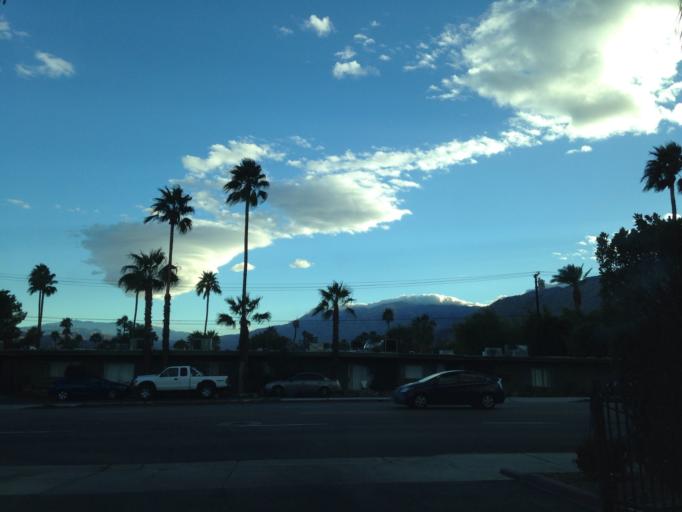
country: US
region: California
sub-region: Riverside County
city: Palm Springs
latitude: 33.8451
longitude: -116.5424
